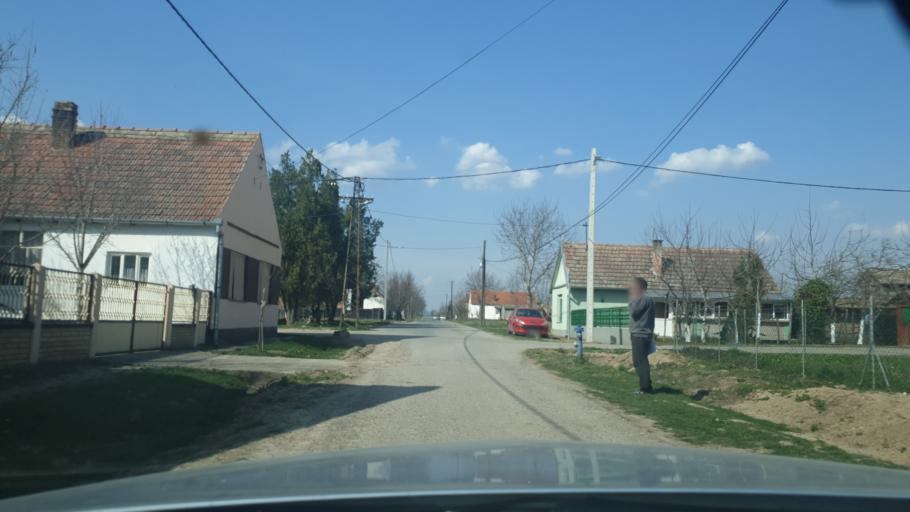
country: RS
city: Putinci
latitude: 45.0414
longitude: 19.9398
